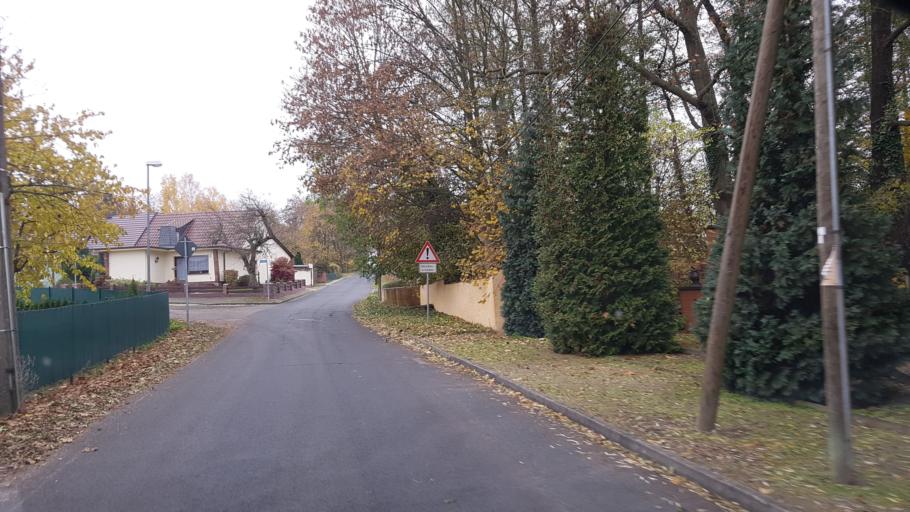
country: DE
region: Brandenburg
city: Crinitz
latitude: 51.7371
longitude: 13.7604
